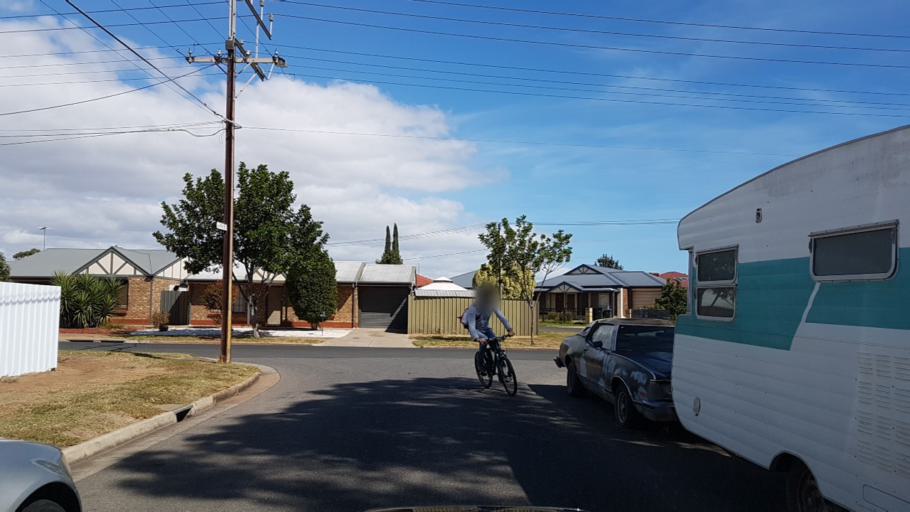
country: AU
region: South Australia
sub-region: Charles Sturt
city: Woodville North
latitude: -34.8554
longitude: 138.5427
